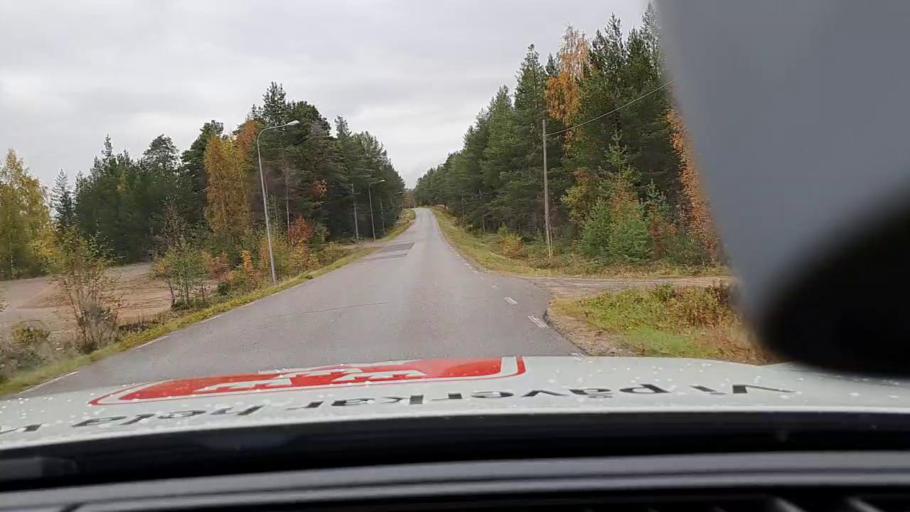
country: SE
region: Norrbotten
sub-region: Haparanda Kommun
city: Haparanda
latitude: 65.7819
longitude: 23.9188
